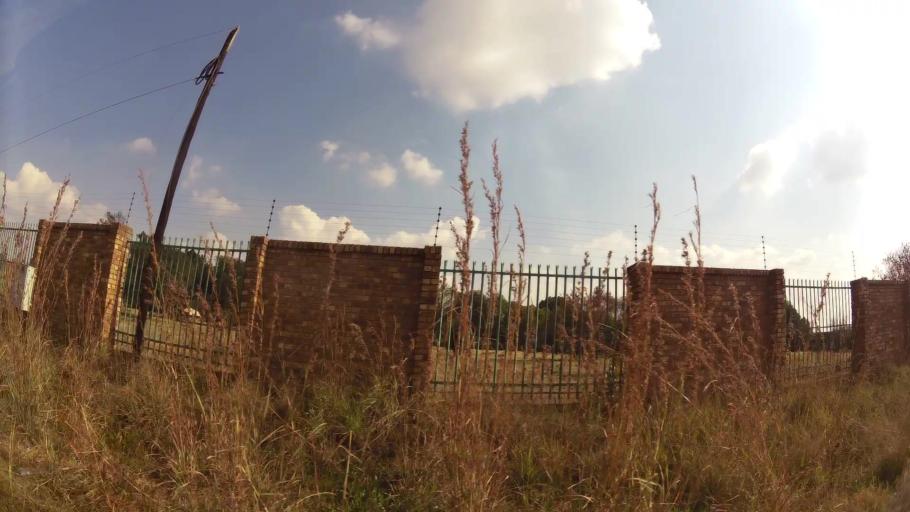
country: ZA
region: Mpumalanga
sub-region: Nkangala District Municipality
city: Delmas
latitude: -26.1843
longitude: 28.5403
